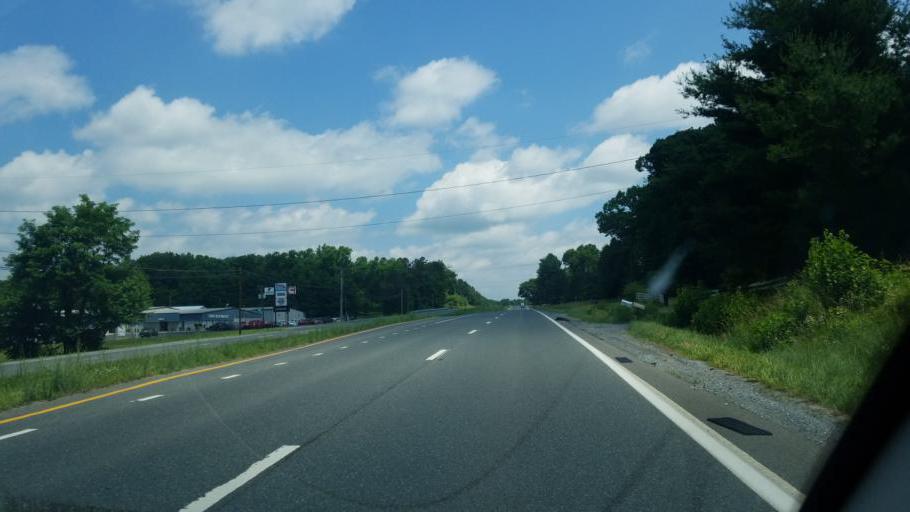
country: US
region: Virginia
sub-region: Campbell County
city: Altavista
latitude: 37.2014
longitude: -79.2031
